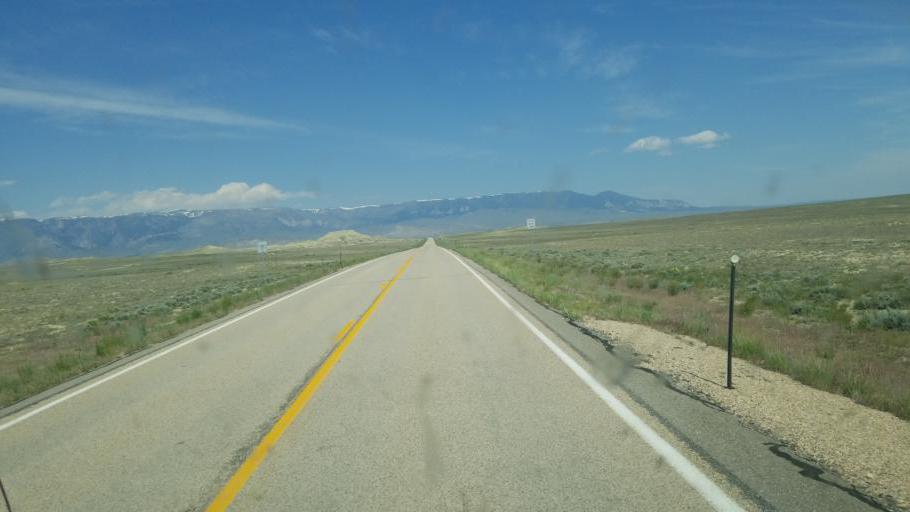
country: US
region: Wyoming
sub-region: Park County
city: Powell
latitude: 44.8777
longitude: -109.0577
